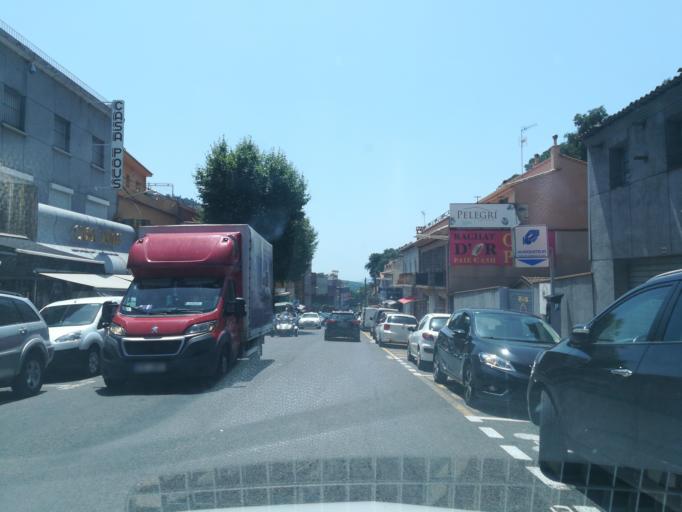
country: ES
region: Catalonia
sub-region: Provincia de Girona
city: la Jonquera
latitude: 42.4622
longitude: 2.8637
